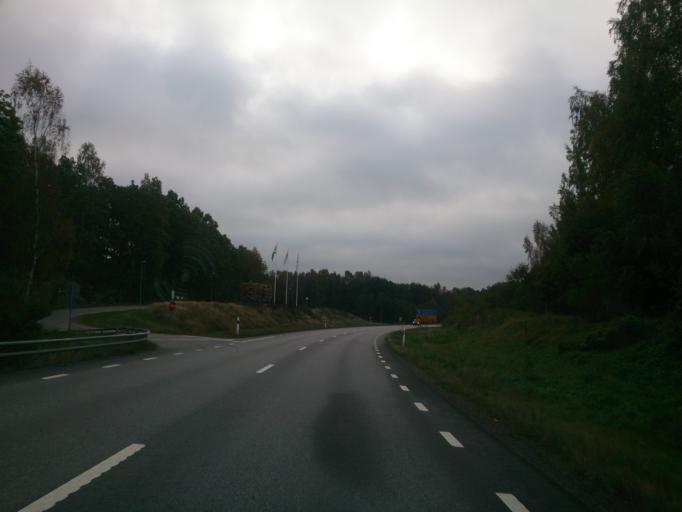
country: SE
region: OEstergoetland
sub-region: Atvidabergs Kommun
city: Atvidaberg
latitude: 58.1959
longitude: 16.0177
